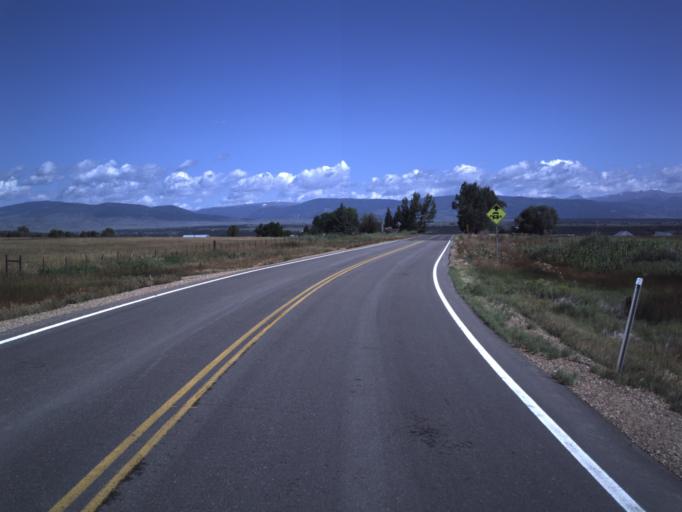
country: US
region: Utah
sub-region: Duchesne County
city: Duchesne
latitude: 40.3275
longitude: -110.4079
